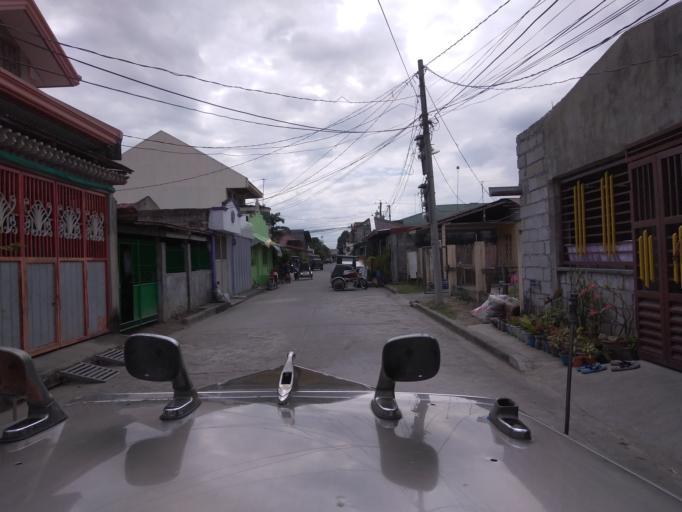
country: PH
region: Central Luzon
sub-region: Province of Pampanga
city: Pandacaqui
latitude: 15.1767
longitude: 120.6474
